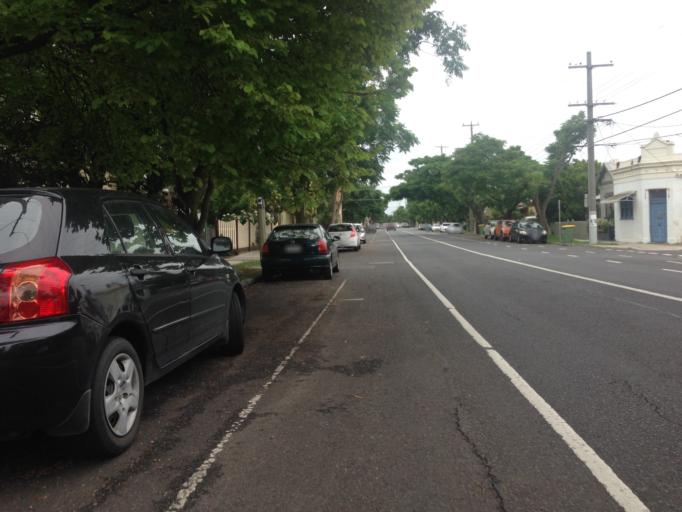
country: AU
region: Victoria
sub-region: Darebin
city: Fairfield
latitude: -37.7823
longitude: 145.0076
